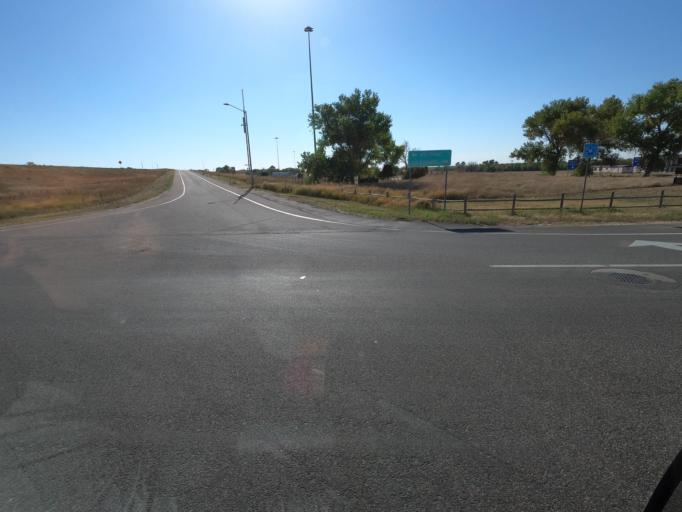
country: US
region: Colorado
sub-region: Sedgwick County
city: Julesburg
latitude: 40.9689
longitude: -102.2478
